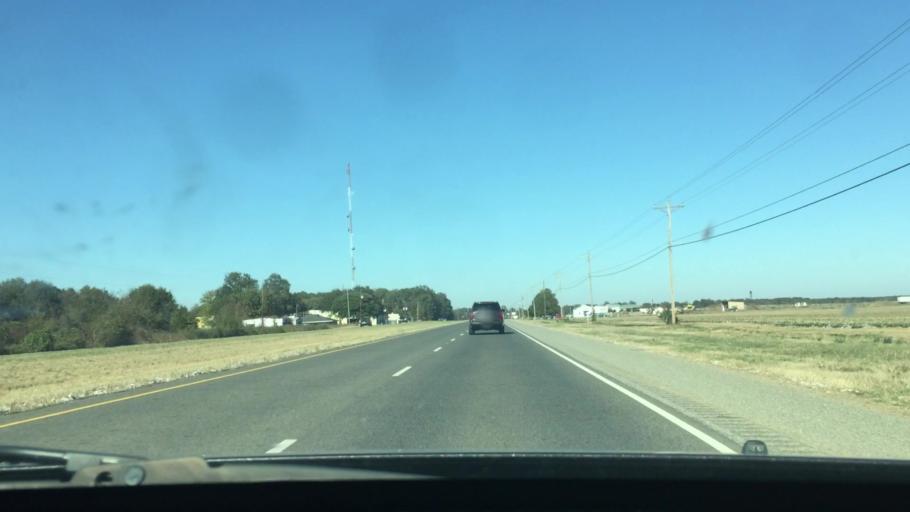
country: US
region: Louisiana
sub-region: Richland Parish
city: Rayville
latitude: 32.4157
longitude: -91.7647
